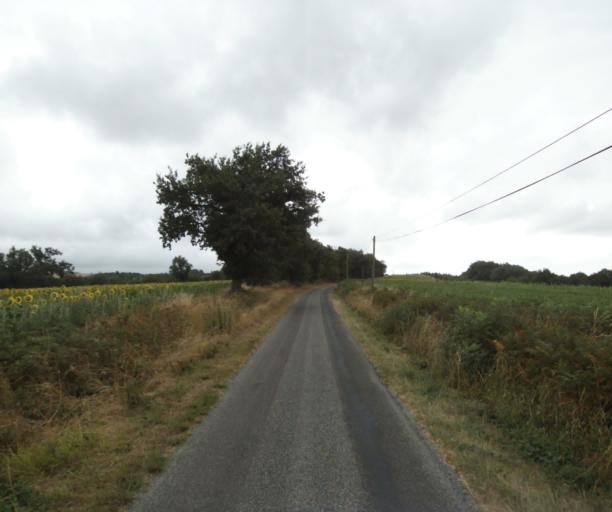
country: FR
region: Midi-Pyrenees
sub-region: Departement du Tarn
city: Soreze
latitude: 43.3893
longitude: 2.0343
